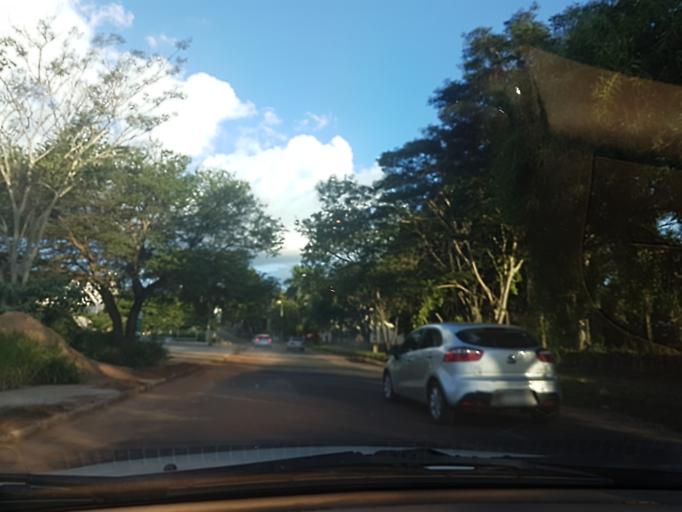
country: PY
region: Asuncion
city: Asuncion
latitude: -25.2810
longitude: -57.5766
